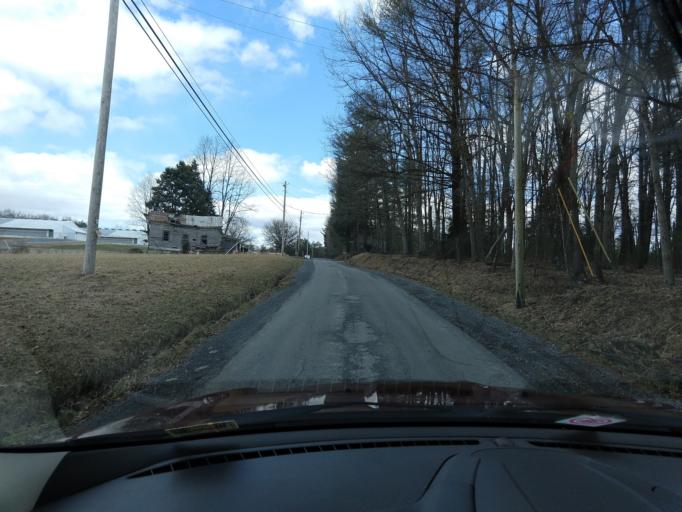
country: US
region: West Virginia
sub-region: Greenbrier County
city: Fairlea
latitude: 37.8279
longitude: -80.5313
